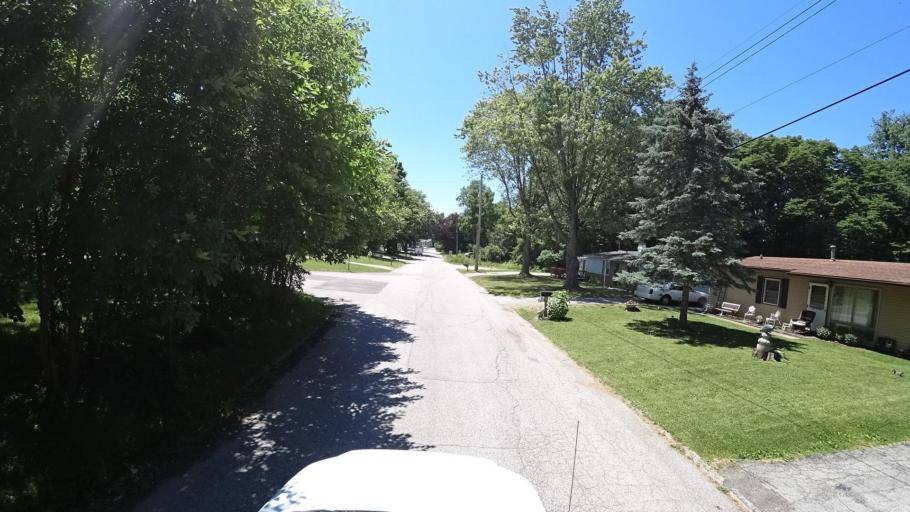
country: US
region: Indiana
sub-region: Porter County
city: Chesterton
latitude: 41.6185
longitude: -87.0602
